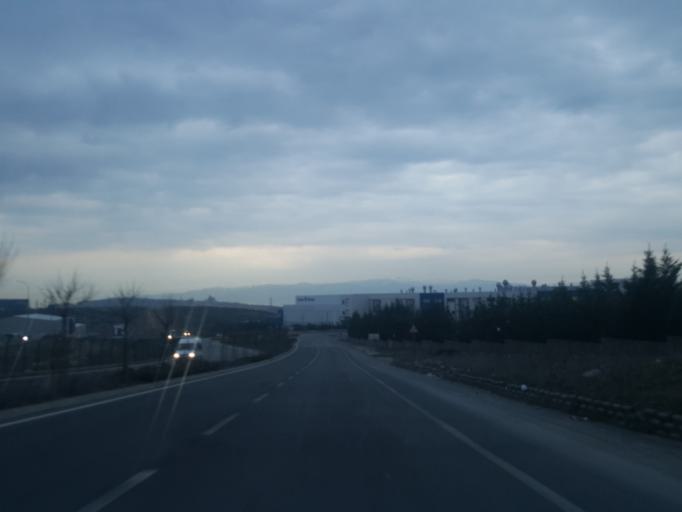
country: TR
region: Kocaeli
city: Tavsanli
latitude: 40.8206
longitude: 29.5607
